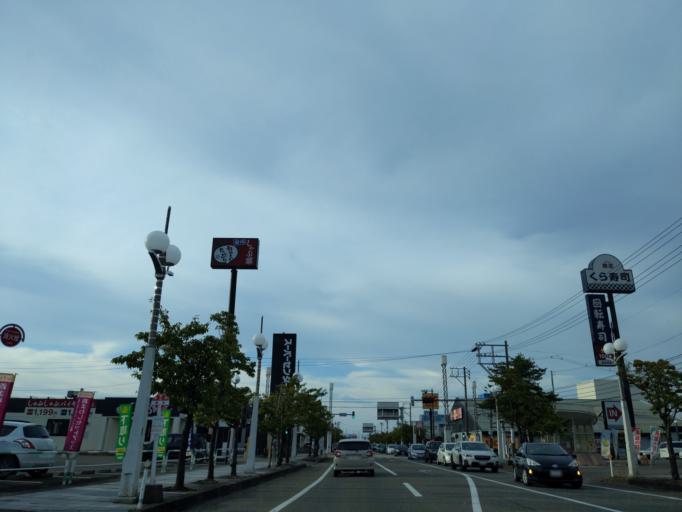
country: JP
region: Niigata
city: Joetsu
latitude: 37.1541
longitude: 138.2550
